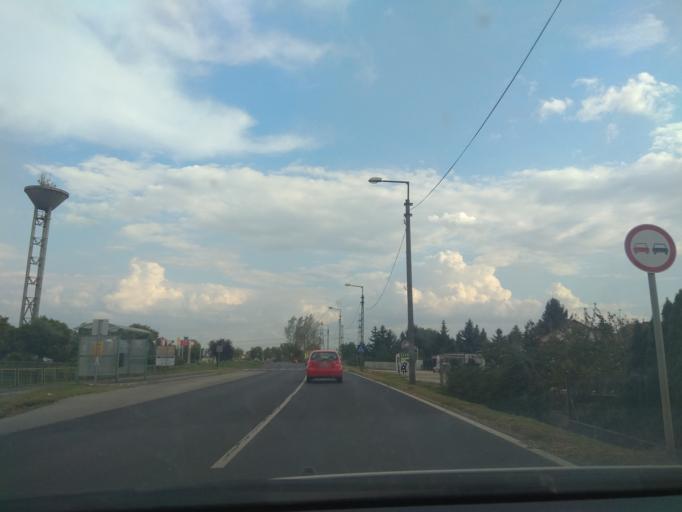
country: HU
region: Borsod-Abauj-Zemplen
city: Sajoszoged
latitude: 47.9434
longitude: 20.9974
